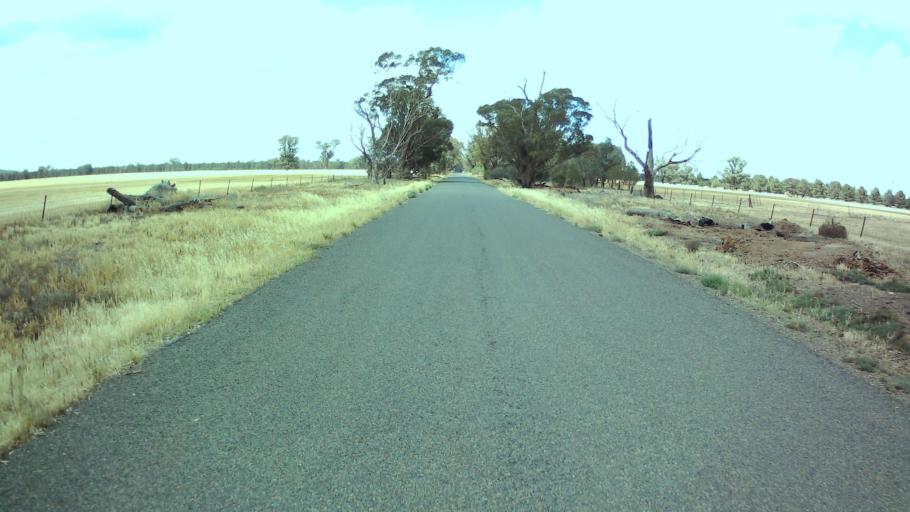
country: AU
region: New South Wales
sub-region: Weddin
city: Grenfell
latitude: -33.8882
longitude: 147.9231
